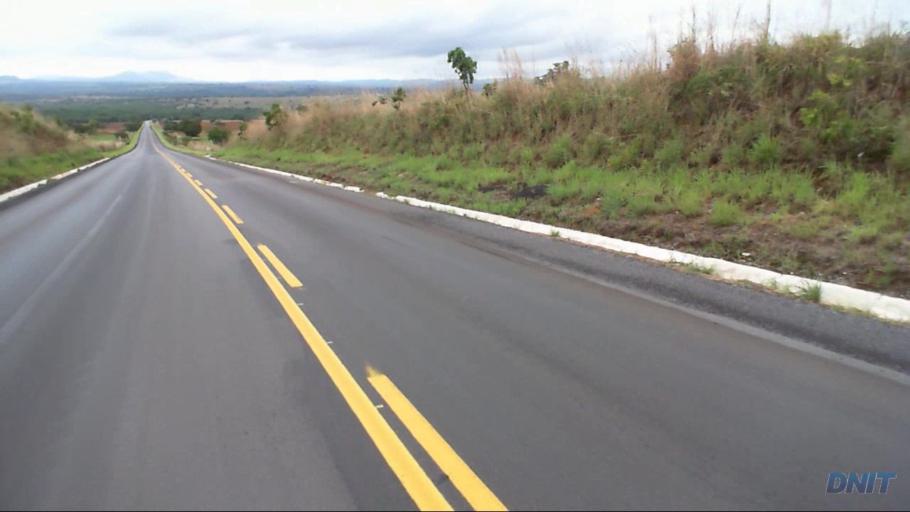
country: BR
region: Goias
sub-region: Padre Bernardo
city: Padre Bernardo
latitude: -15.2198
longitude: -48.5307
